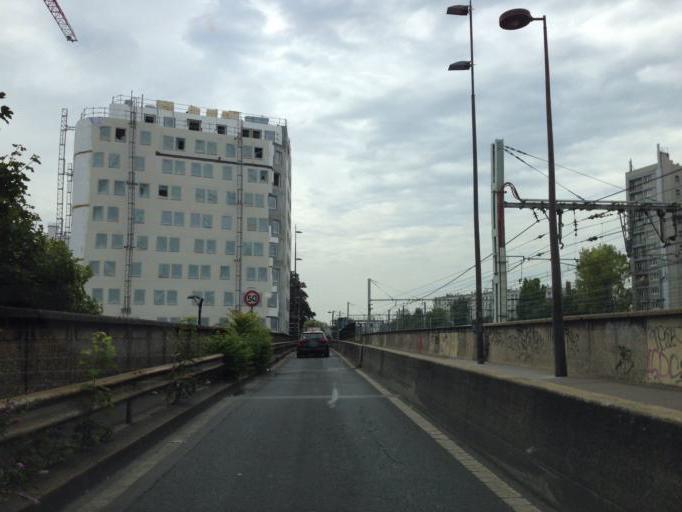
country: FR
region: Ile-de-France
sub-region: Departement des Hauts-de-Seine
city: Malakoff
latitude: 48.8282
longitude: 2.3051
